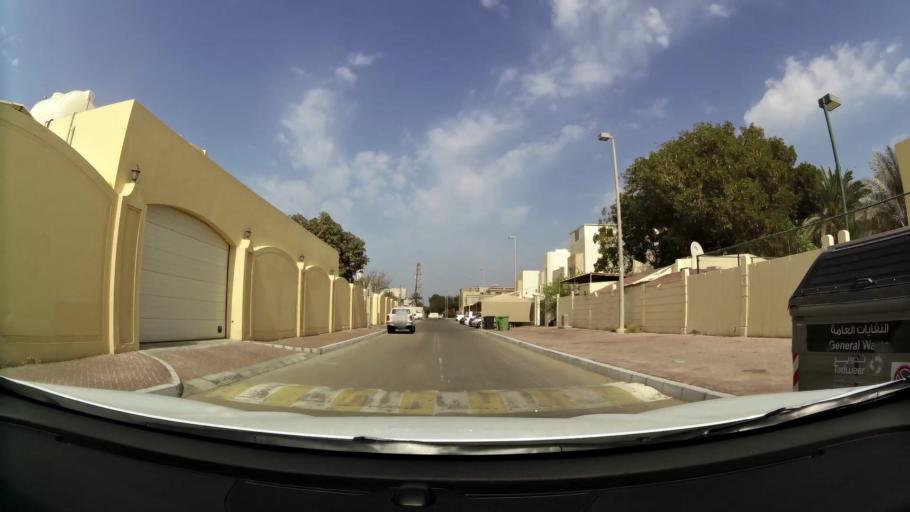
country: AE
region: Abu Dhabi
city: Abu Dhabi
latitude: 24.4330
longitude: 54.3709
